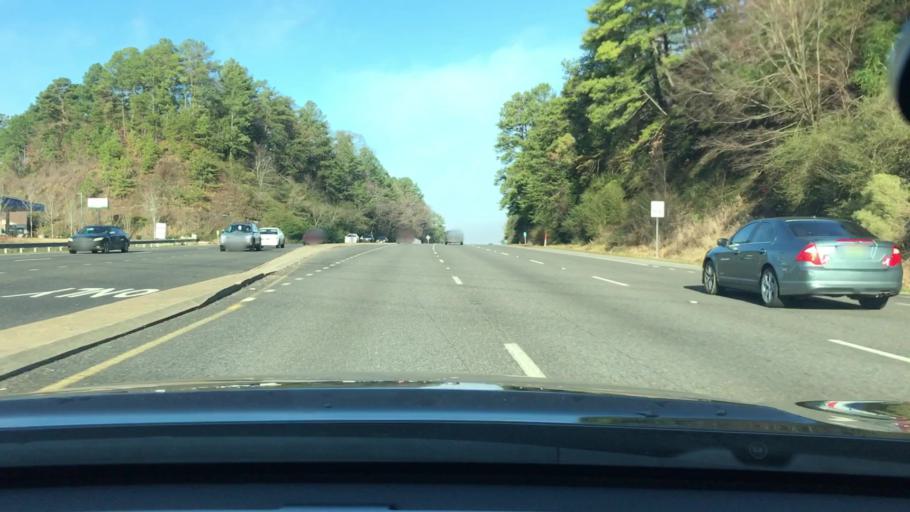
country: US
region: Alabama
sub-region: Jefferson County
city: Cahaba Heights
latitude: 33.4458
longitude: -86.7359
